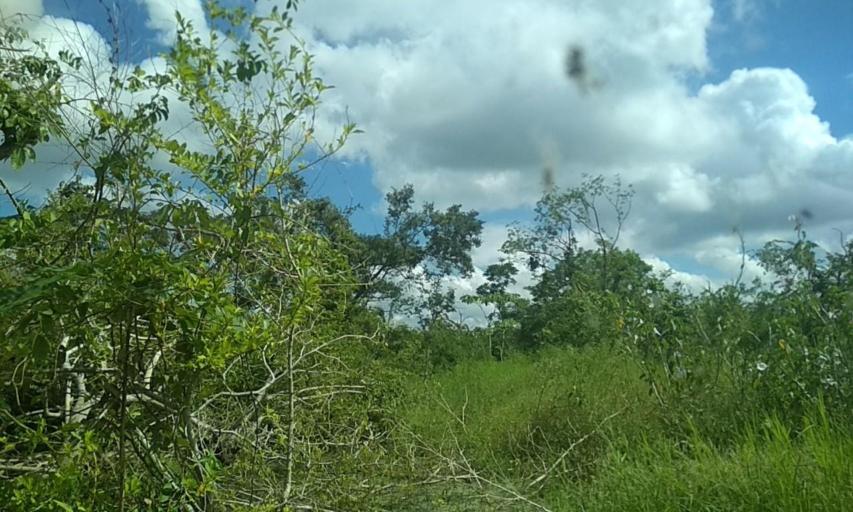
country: MX
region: Veracruz
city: Gutierrez Zamora
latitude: 20.2847
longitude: -97.1286
